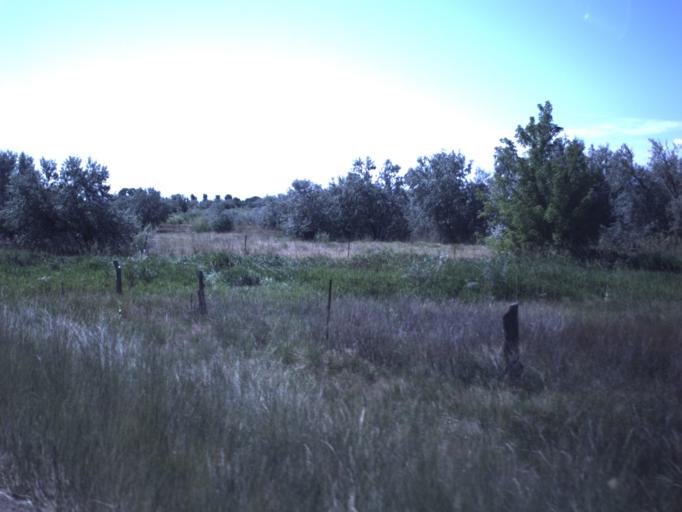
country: US
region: Utah
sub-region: Duchesne County
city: Duchesne
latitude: 40.3235
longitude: -110.2621
